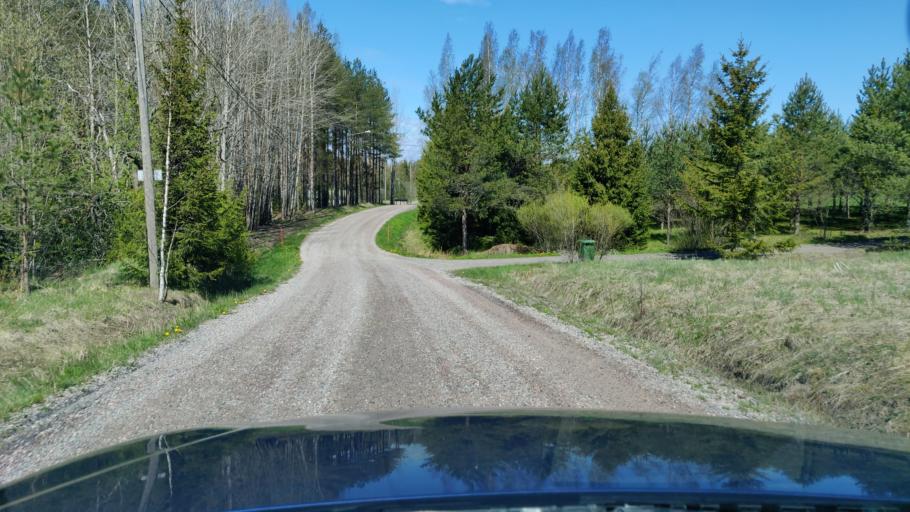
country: FI
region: Uusimaa
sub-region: Helsinki
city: Nurmijaervi
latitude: 60.3554
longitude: 24.7591
